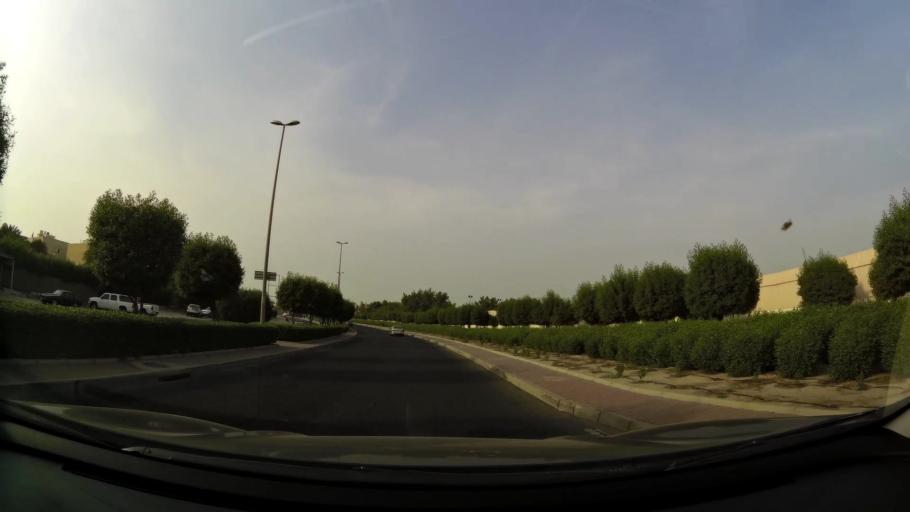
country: KW
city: Al Funaytis
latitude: 29.2146
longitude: 48.0789
